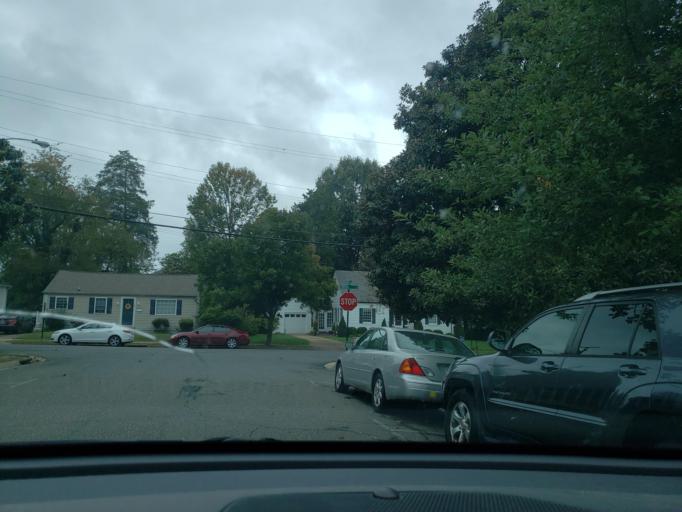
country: US
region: Virginia
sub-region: City of Fredericksburg
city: Fredericksburg
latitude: 38.2993
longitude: -77.4758
